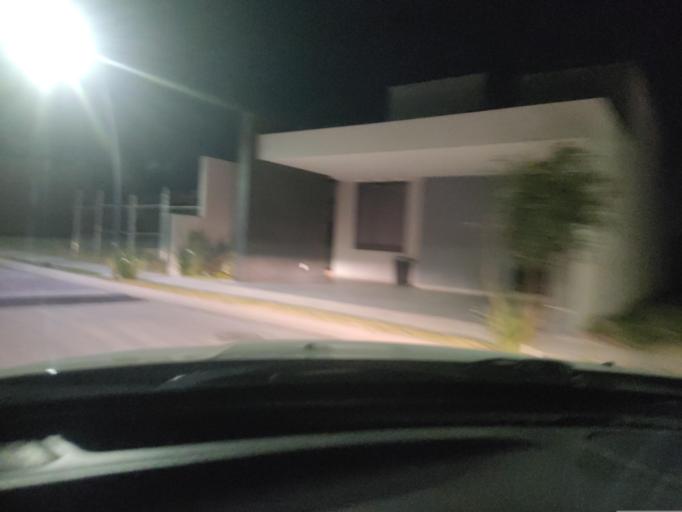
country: MX
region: Guanajuato
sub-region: Leon
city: Ladrilleras del Refugio
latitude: 21.0848
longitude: -101.5620
